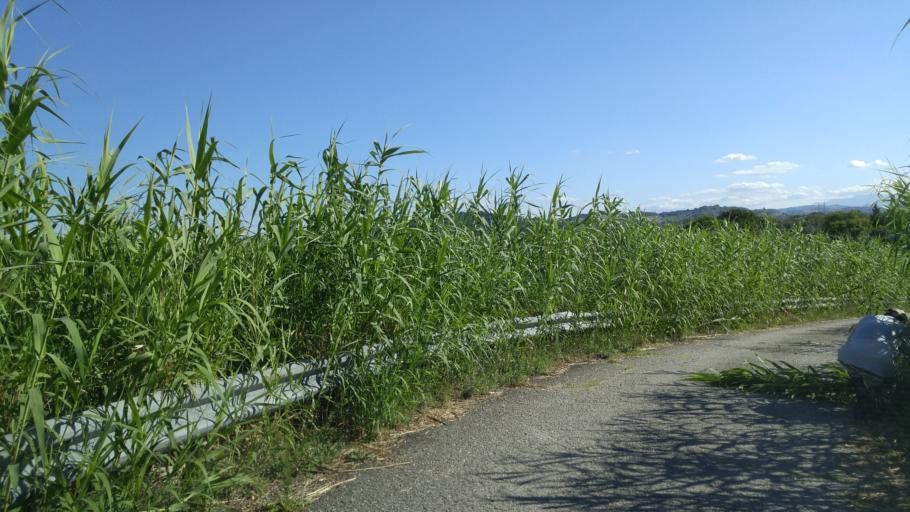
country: IT
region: The Marches
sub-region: Provincia di Pesaro e Urbino
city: Calcinelli
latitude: 43.7521
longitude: 12.9277
